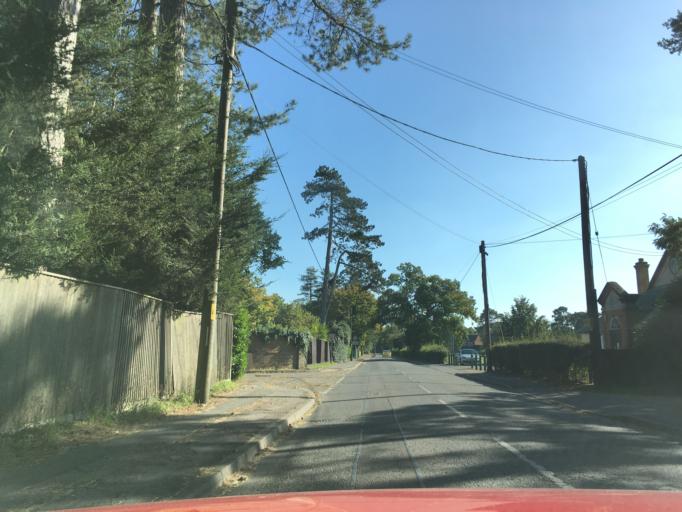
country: GB
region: England
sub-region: West Berkshire
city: Cold Ash
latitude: 51.4303
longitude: -1.2681
